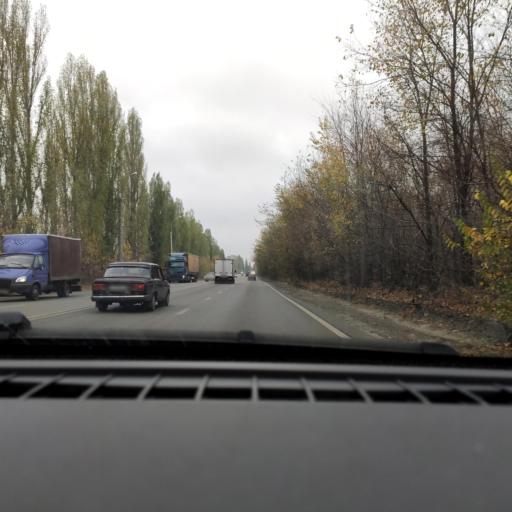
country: RU
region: Voronezj
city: Maslovka
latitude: 51.6080
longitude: 39.2557
